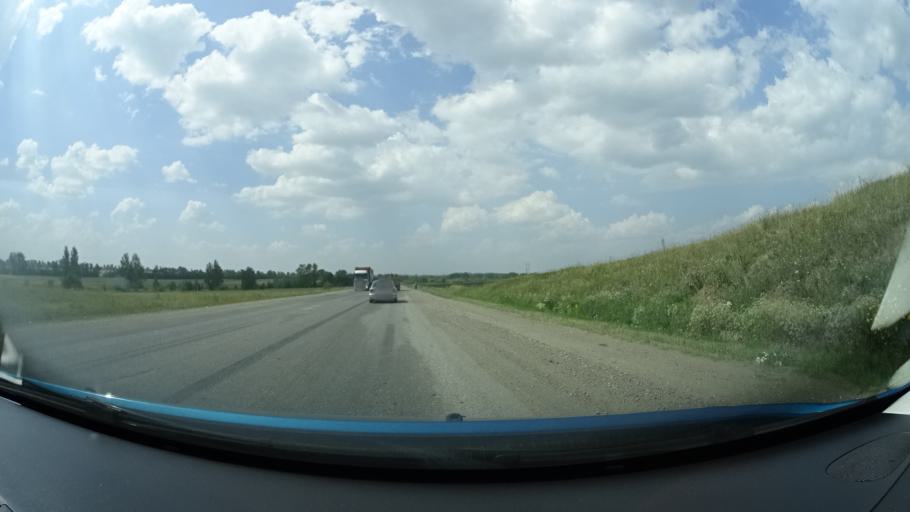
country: RU
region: Bashkortostan
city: Kandry
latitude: 54.5140
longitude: 53.9788
